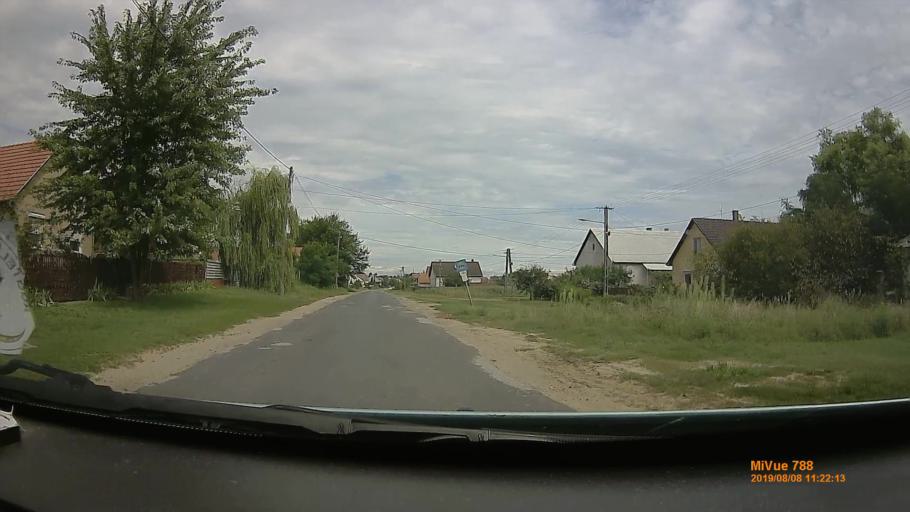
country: HU
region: Szabolcs-Szatmar-Bereg
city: Balkany
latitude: 47.7598
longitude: 21.8481
